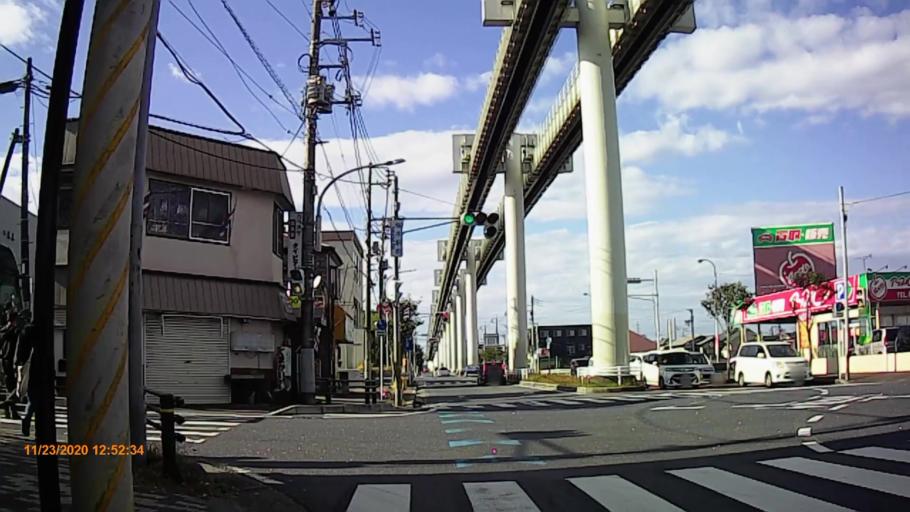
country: JP
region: Chiba
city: Yotsukaido
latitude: 35.6316
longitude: 140.1600
